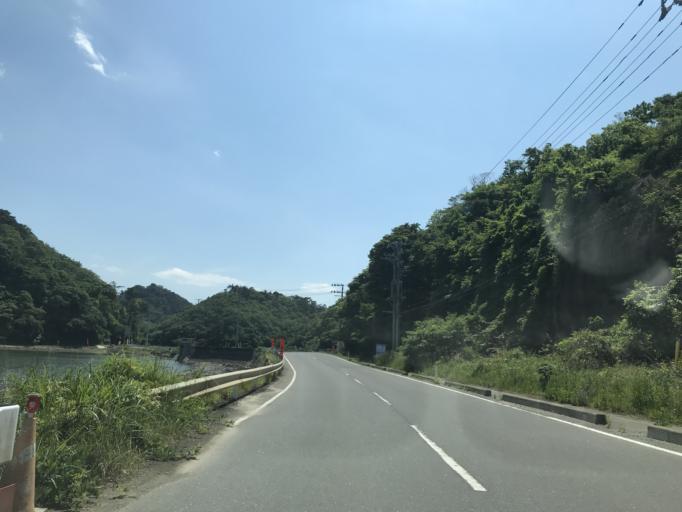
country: JP
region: Miyagi
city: Matsushima
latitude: 38.3499
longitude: 141.1546
